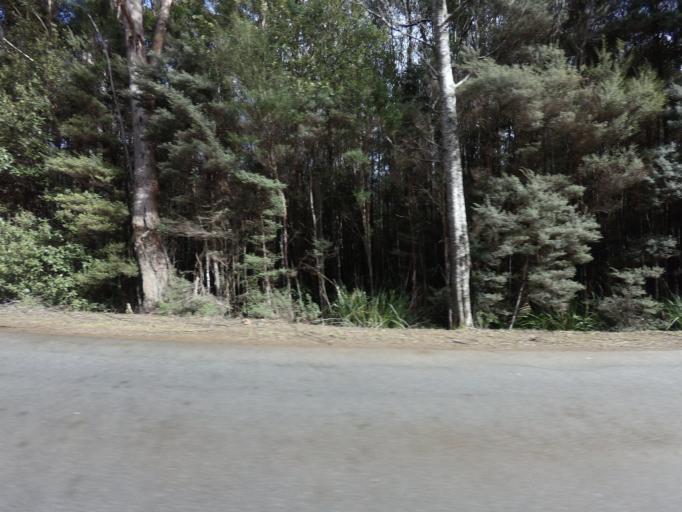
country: AU
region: Tasmania
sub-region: Huon Valley
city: Geeveston
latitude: -43.3749
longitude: 146.9556
